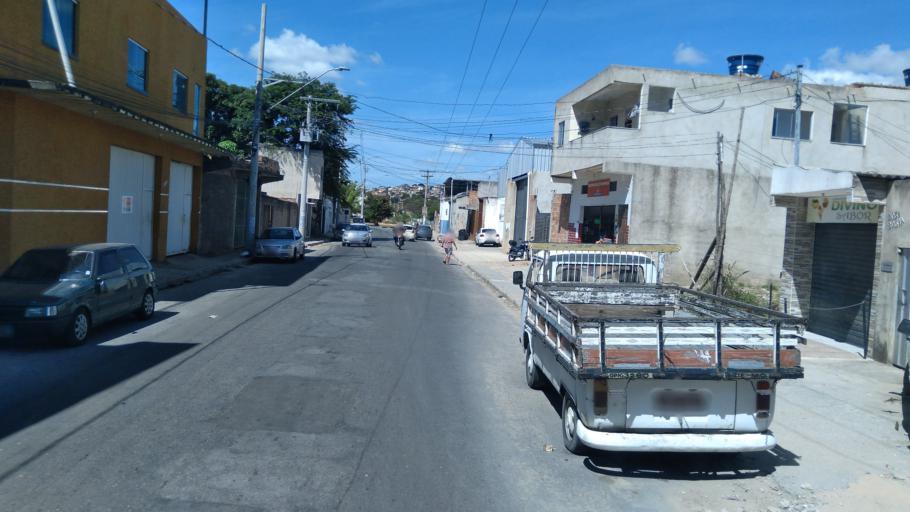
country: BR
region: Minas Gerais
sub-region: Belo Horizonte
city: Belo Horizonte
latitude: -19.8467
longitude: -43.9143
